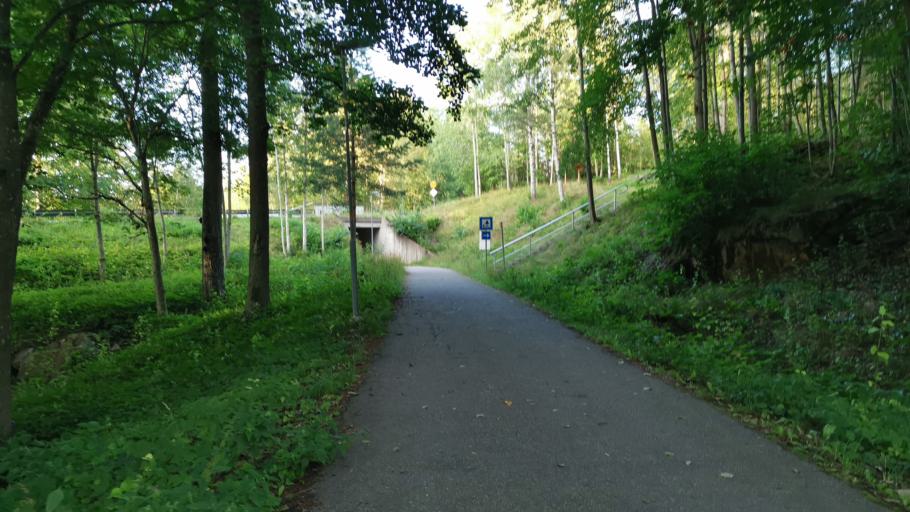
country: SE
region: OEstergoetland
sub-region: Norrkopings Kommun
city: Krokek
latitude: 58.7254
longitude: 16.4284
